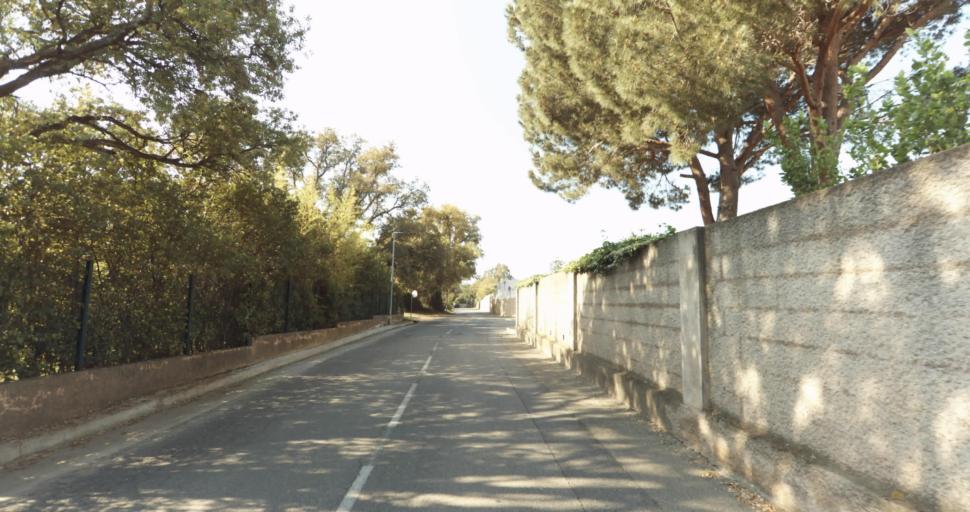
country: FR
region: Corsica
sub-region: Departement de la Haute-Corse
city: Biguglia
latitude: 42.6358
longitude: 9.4341
